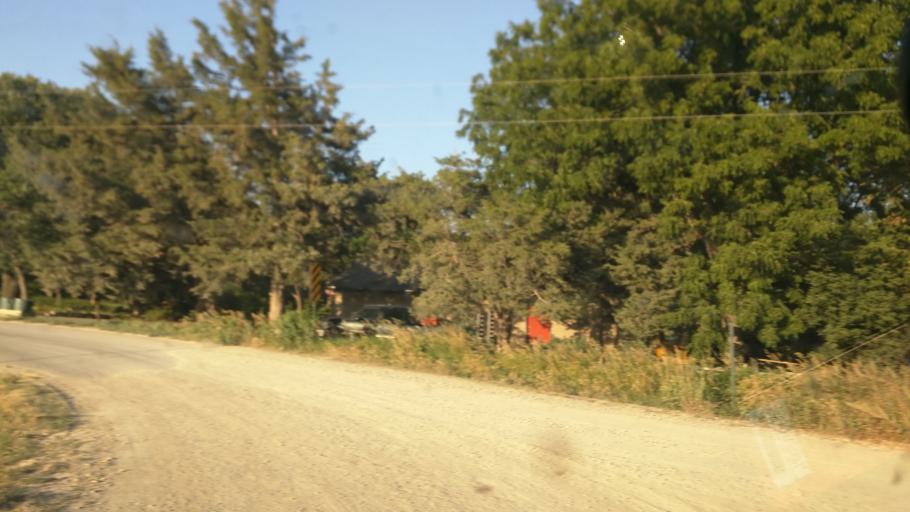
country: US
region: Kansas
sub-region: Riley County
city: Manhattan
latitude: 39.2617
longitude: -96.6820
